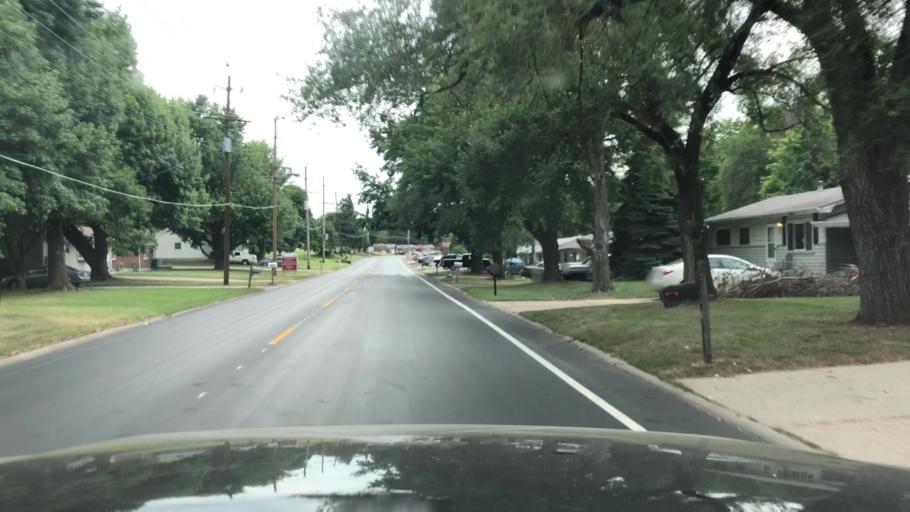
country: US
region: Missouri
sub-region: Saint Charles County
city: Saint Charles
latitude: 38.7738
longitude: -90.5042
